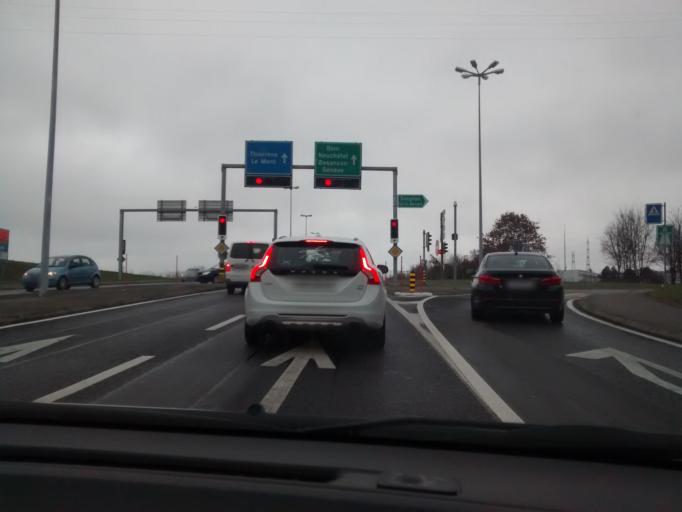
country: CH
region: Vaud
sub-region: Lausanne District
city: Blecherette
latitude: 46.5483
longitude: 6.6240
